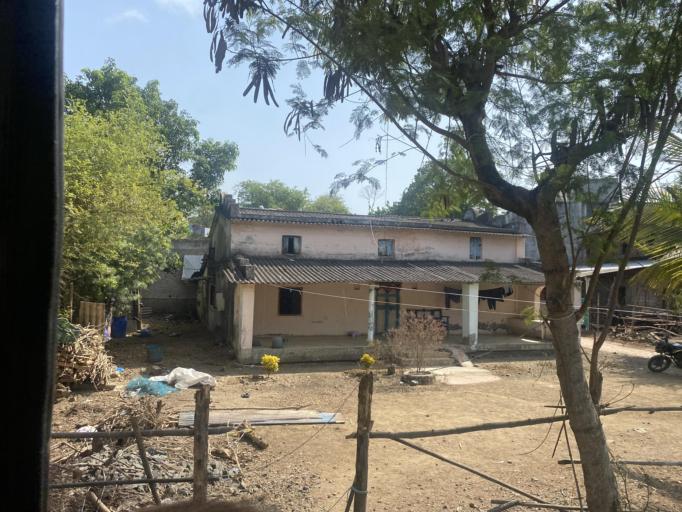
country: IN
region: Daman and Diu
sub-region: Daman District
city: Daman
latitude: 20.3348
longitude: 72.8052
